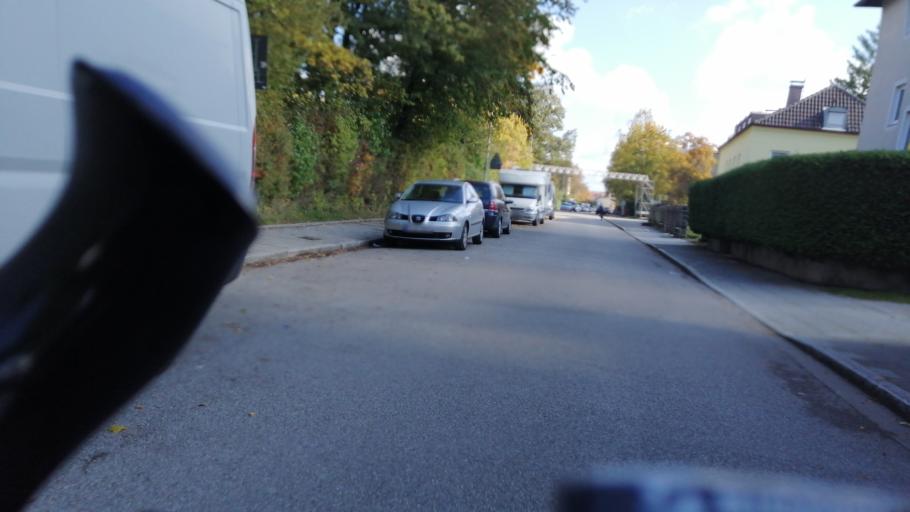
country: DE
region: Bavaria
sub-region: Upper Bavaria
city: Pasing
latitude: 48.1343
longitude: 11.4936
